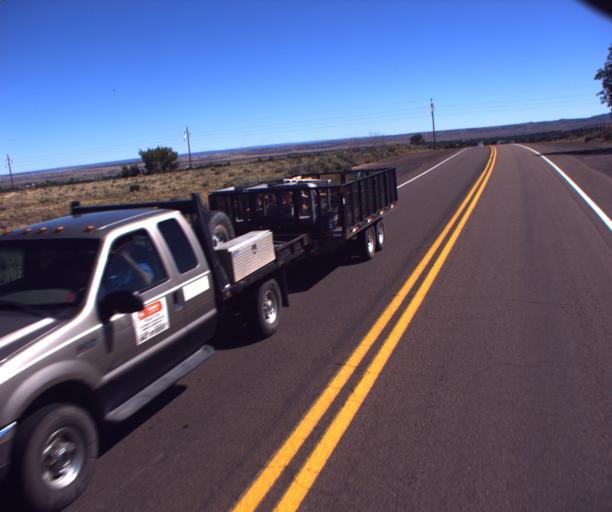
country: US
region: Arizona
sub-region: Apache County
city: Saint Johns
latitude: 34.5060
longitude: -109.4127
